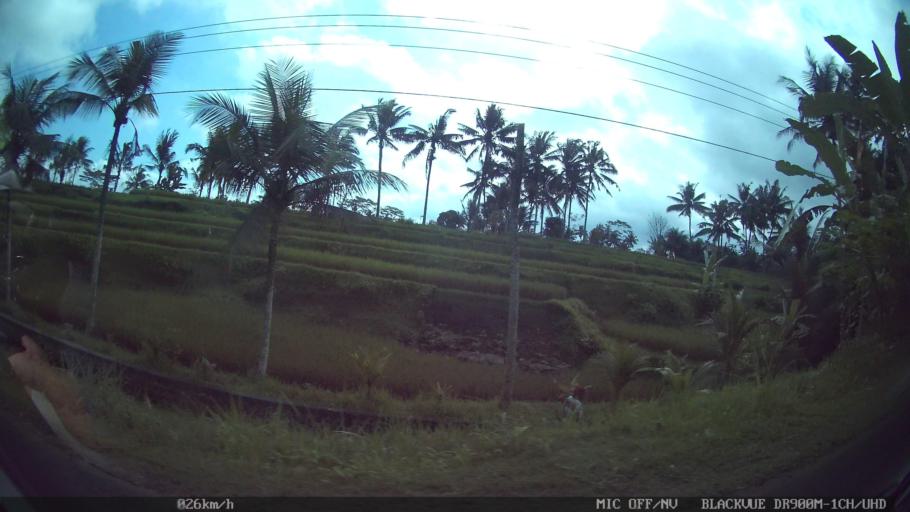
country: ID
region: Bali
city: Banjar Pesalakan
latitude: -8.4836
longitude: 115.2974
